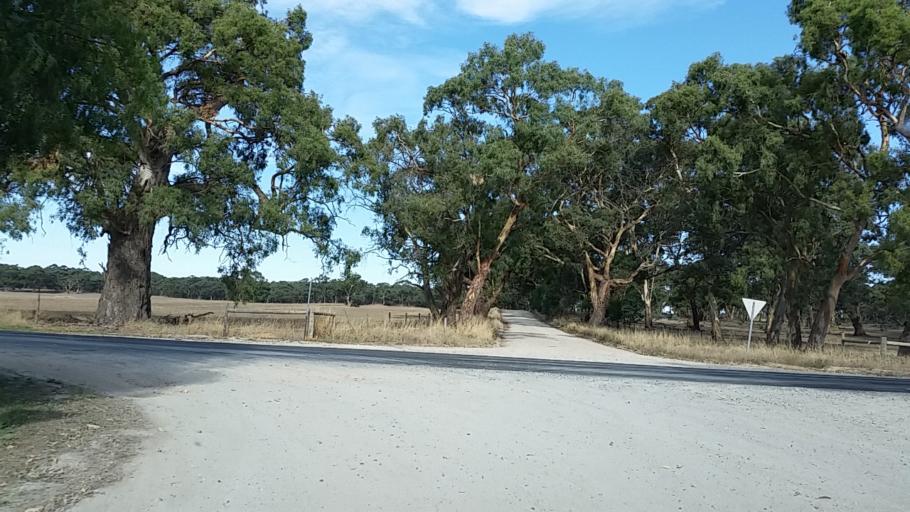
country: AU
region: South Australia
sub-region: Barossa
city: Angaston
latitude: -34.5744
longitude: 139.1254
